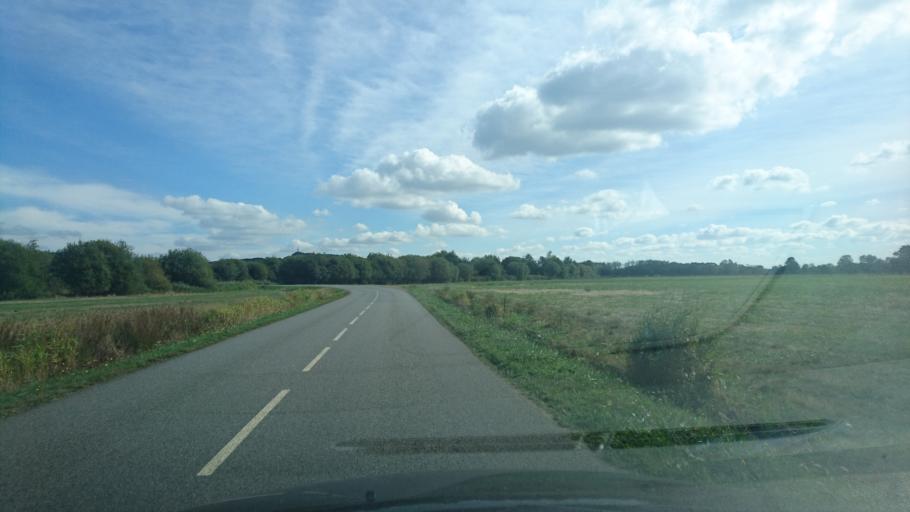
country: FR
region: Brittany
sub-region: Departement du Morbihan
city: Saint-Perreux
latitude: 47.6607
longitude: -2.1183
